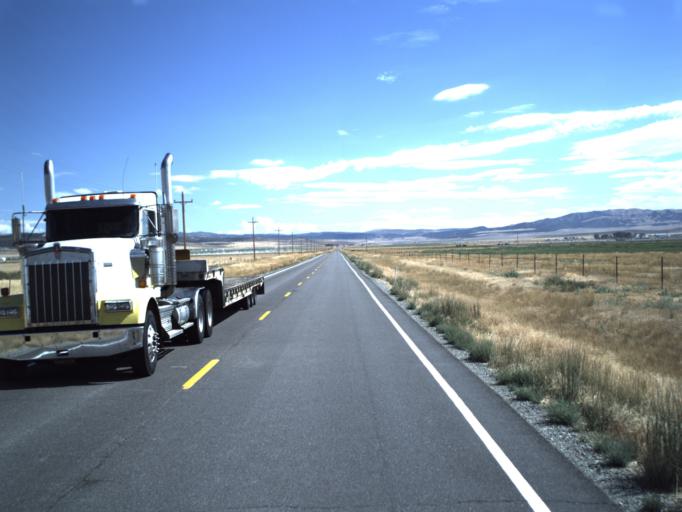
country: US
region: Idaho
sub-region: Oneida County
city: Malad City
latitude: 41.9670
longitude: -112.8711
